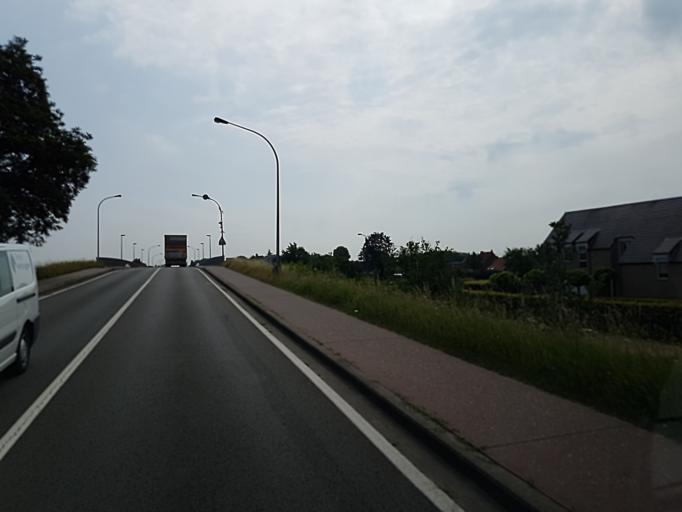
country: BE
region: Flanders
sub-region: Provincie Antwerpen
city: Balen
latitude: 51.1731
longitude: 5.1498
